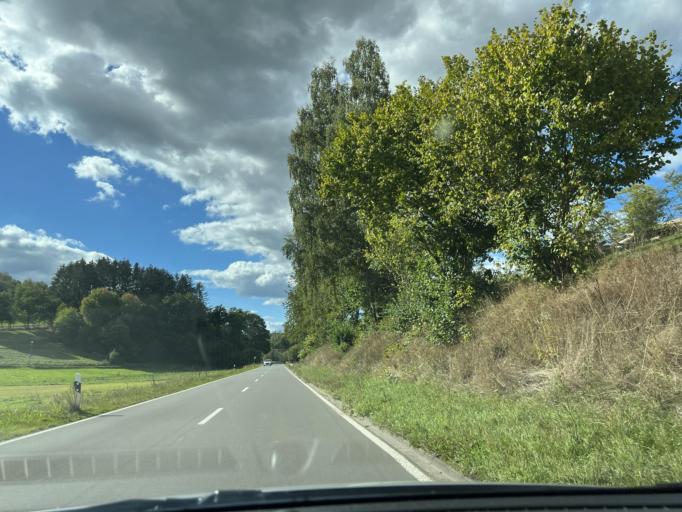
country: DE
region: North Rhine-Westphalia
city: Hilchenbach
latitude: 50.9713
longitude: 8.1263
